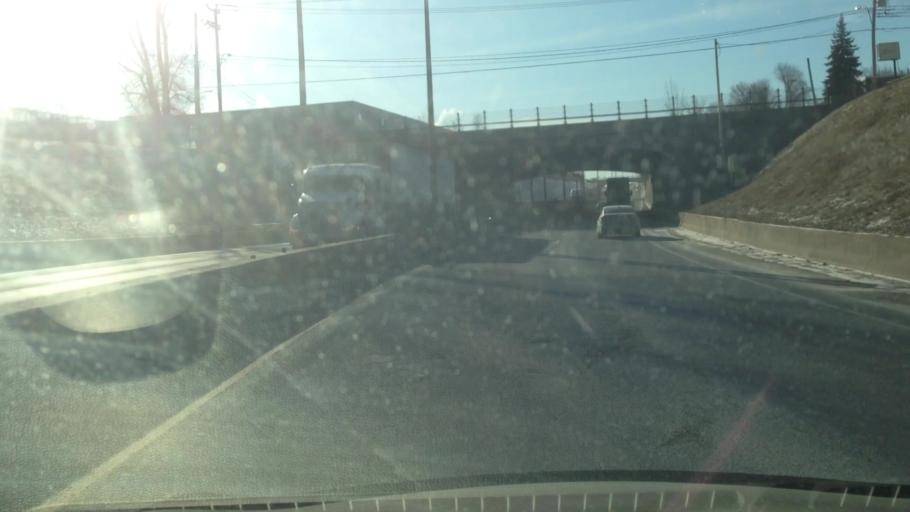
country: CA
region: Quebec
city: Montreal-Ouest
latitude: 45.4294
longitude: -73.6494
